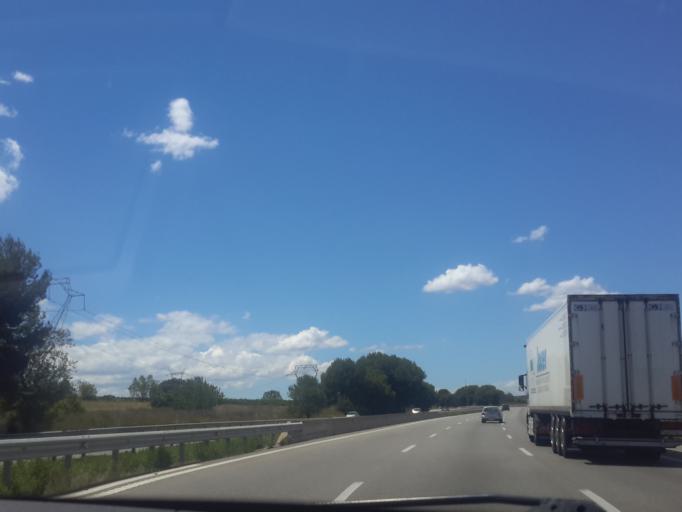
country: ES
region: Catalonia
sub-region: Provincia de Barcelona
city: La Granada
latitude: 41.3868
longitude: 1.7528
